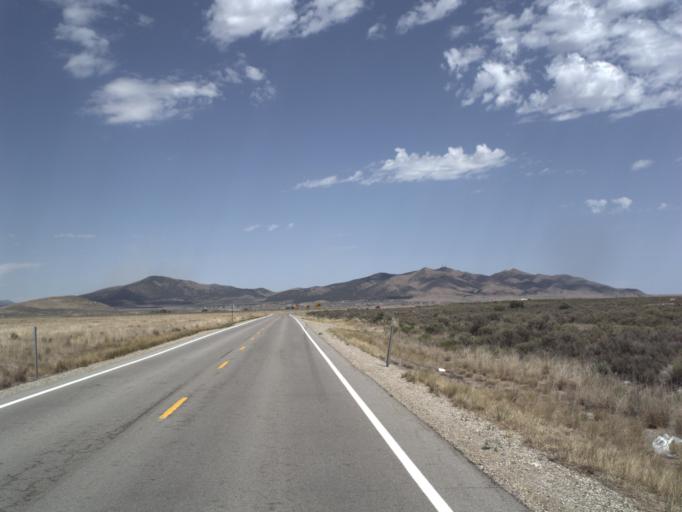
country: US
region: Utah
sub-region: Tooele County
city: Tooele
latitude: 40.3565
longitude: -112.4133
